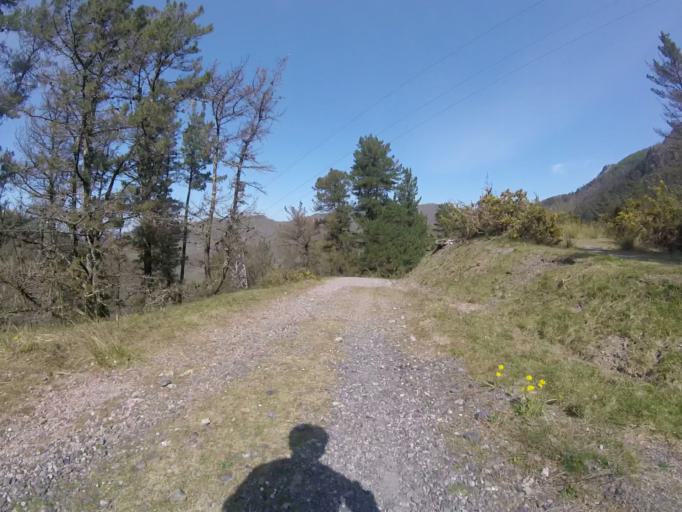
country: ES
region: Basque Country
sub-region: Provincia de Guipuzcoa
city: Irun
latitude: 43.2754
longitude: -1.8063
